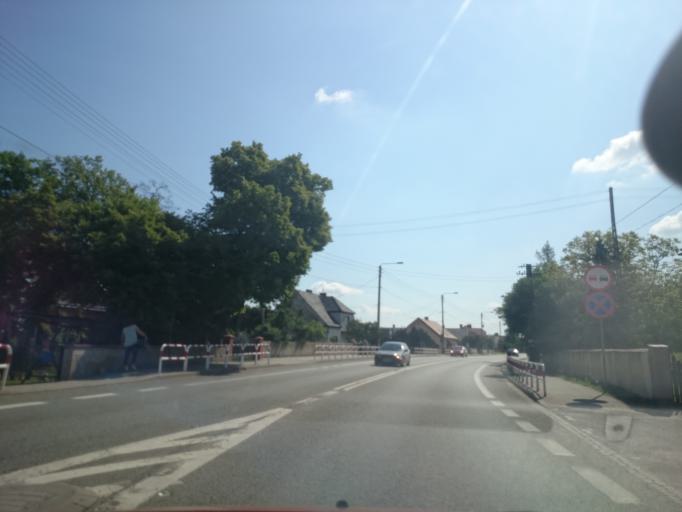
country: PL
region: Opole Voivodeship
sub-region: Powiat opolski
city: Naklo
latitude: 50.5793
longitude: 18.1201
